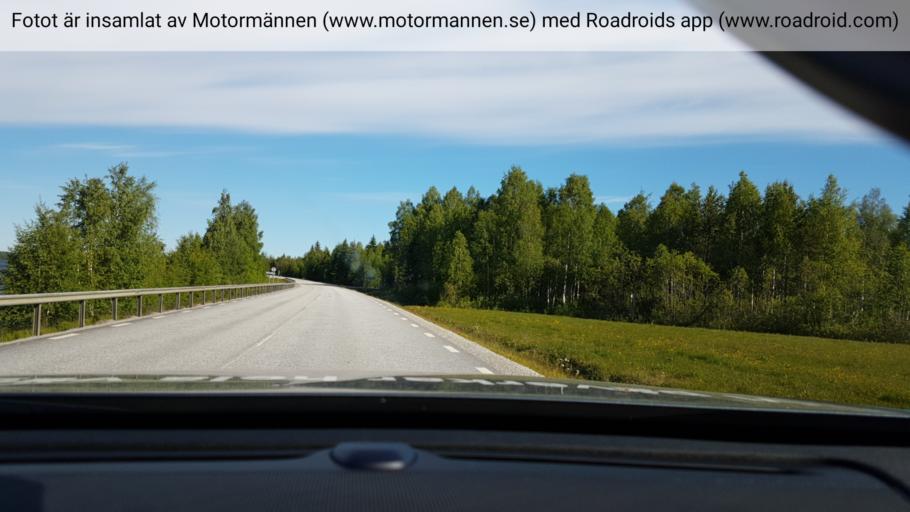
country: SE
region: Vaesterbotten
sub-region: Vindelns Kommun
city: Vindeln
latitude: 64.1814
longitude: 19.4762
